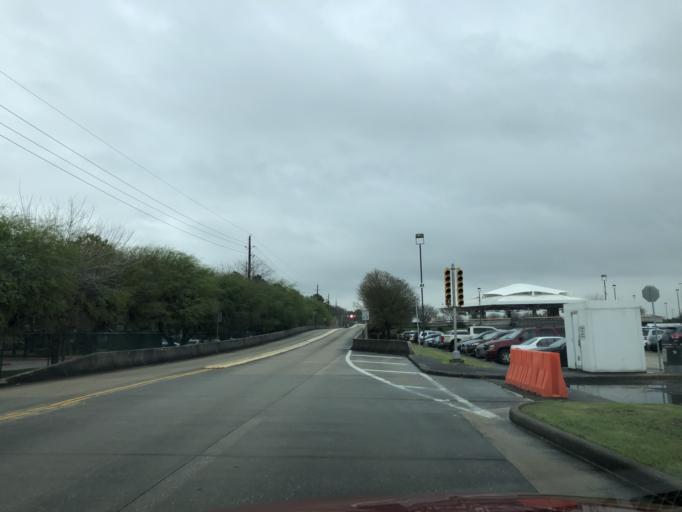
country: US
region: Texas
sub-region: Harris County
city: Aldine
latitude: 29.9740
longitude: -95.4272
